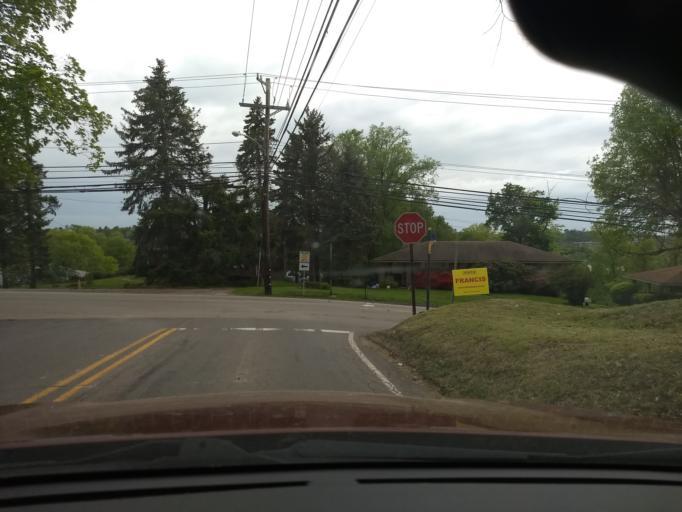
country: US
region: Pennsylvania
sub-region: Allegheny County
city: Rennerdale
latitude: 40.4566
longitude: -80.1382
